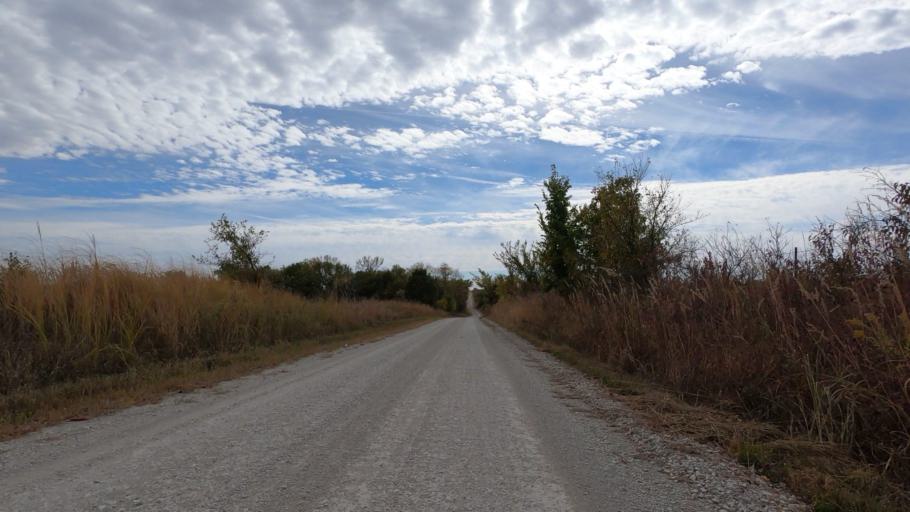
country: US
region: Kansas
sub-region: Pottawatomie County
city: Westmoreland
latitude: 39.3439
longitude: -96.4453
